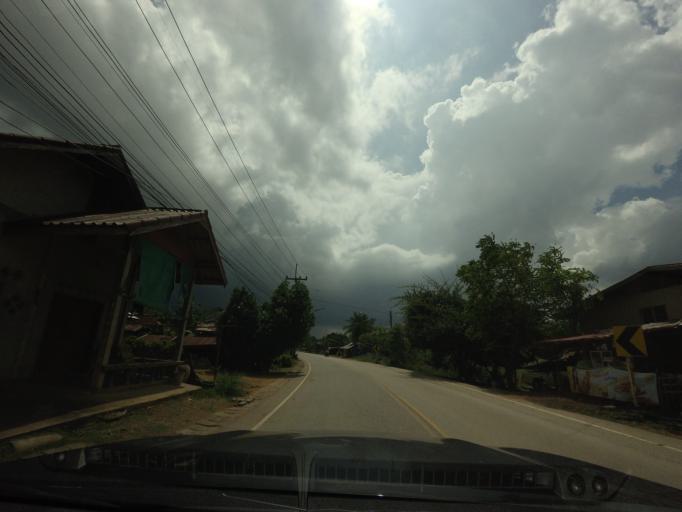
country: LA
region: Vientiane
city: Muang Sanakham
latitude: 17.9919
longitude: 101.7478
